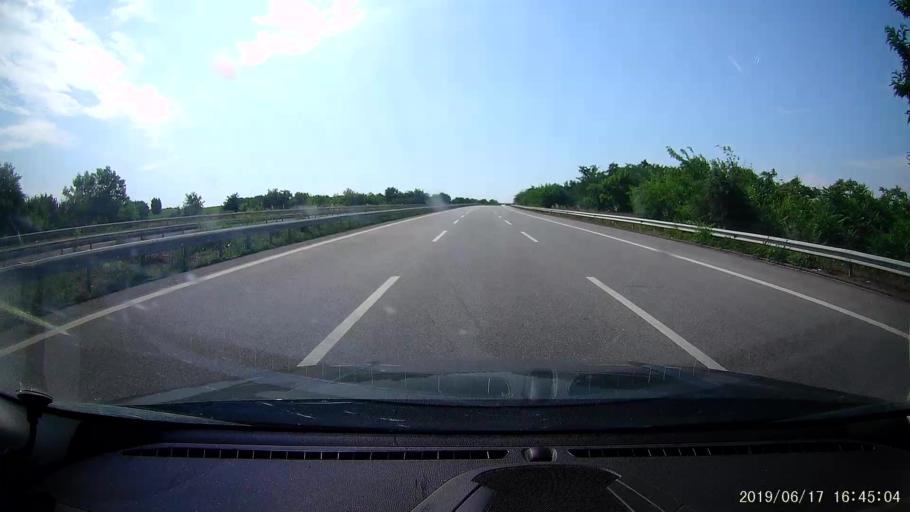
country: TR
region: Kirklareli
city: Luleburgaz
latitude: 41.4842
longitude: 27.2423
